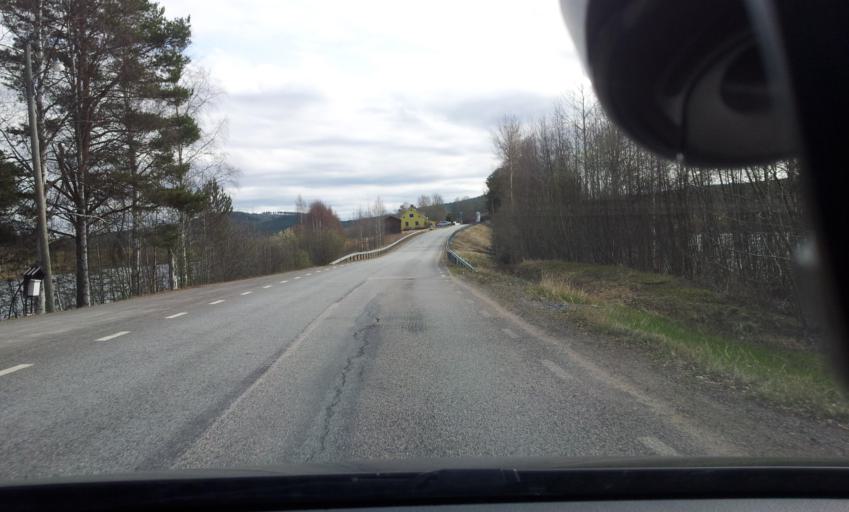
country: SE
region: Gaevleborg
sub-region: Ljusdals Kommun
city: Farila
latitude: 61.7787
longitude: 15.9464
